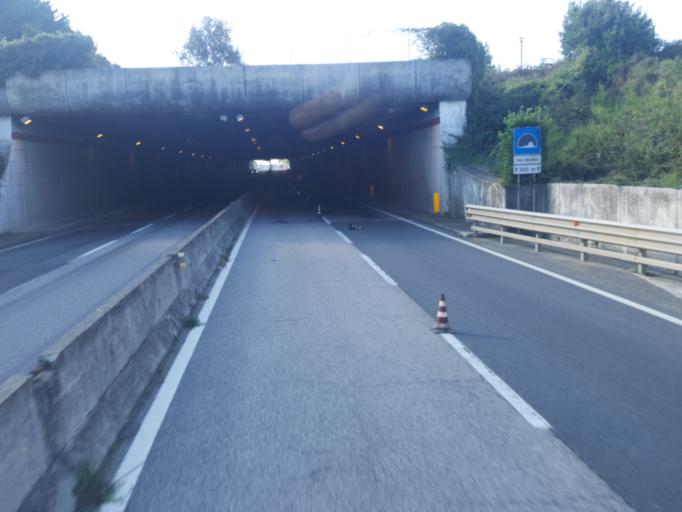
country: IT
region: Tuscany
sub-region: Provincia di Livorno
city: Livorno
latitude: 43.5201
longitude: 10.3315
